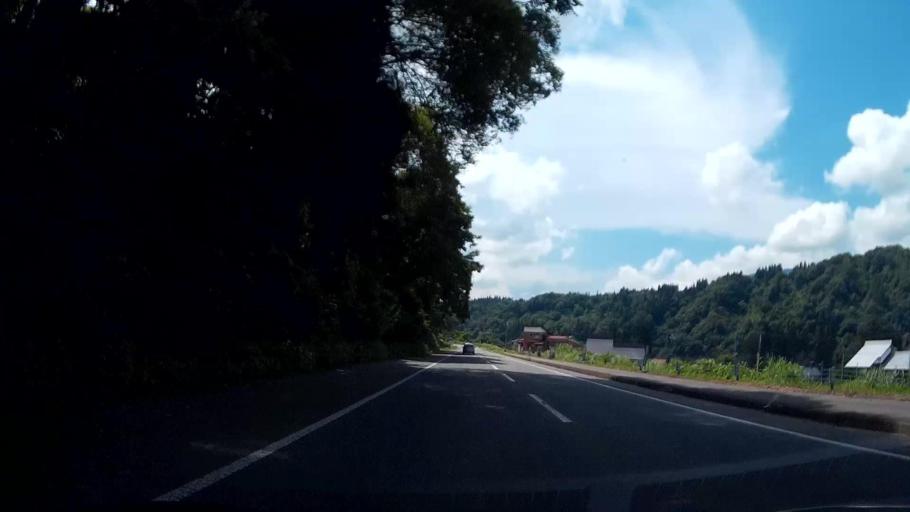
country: JP
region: Niigata
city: Tokamachi
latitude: 36.9997
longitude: 138.6207
